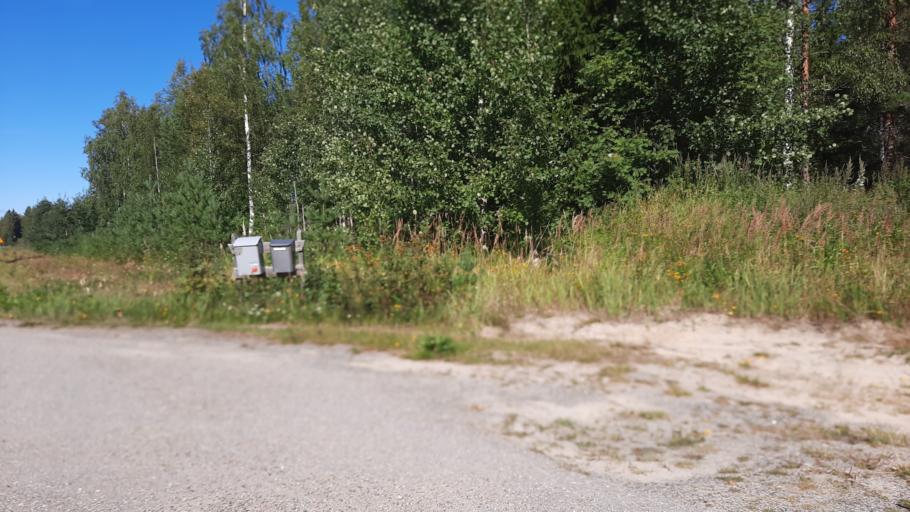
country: FI
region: North Karelia
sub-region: Joensuu
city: Joensuu
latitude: 62.6308
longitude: 29.7343
